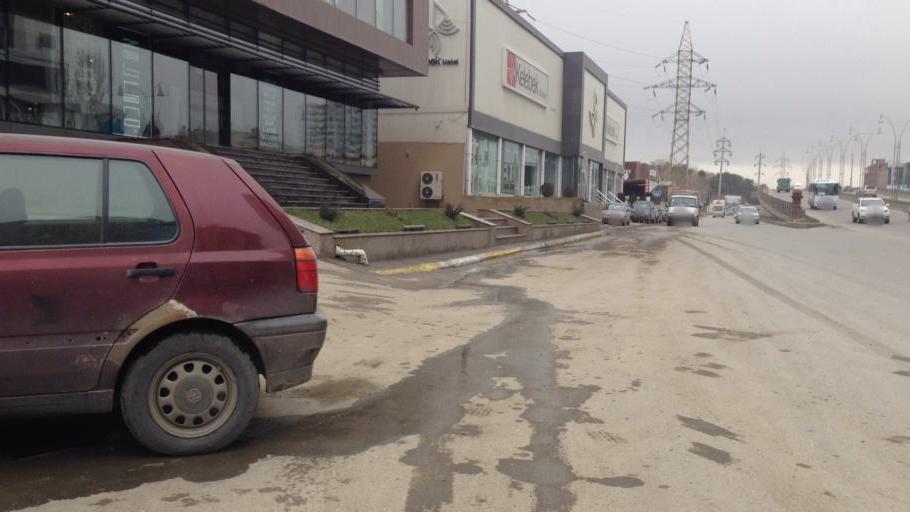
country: AZ
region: Baki
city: Baku
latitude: 40.3891
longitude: 49.8719
